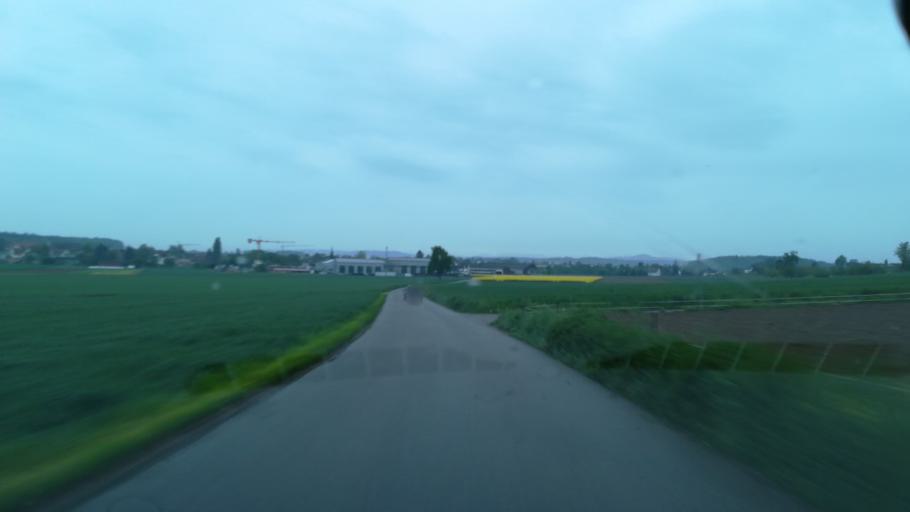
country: CH
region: Zurich
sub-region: Bezirk Buelach
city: End-Hoeri
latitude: 47.5147
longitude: 8.5013
